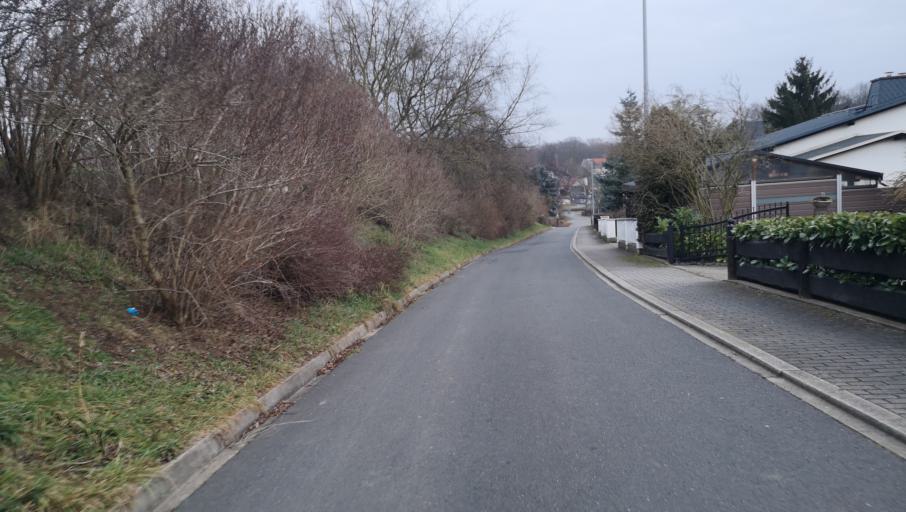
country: DE
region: Thuringia
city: Ronneburg
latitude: 50.8607
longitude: 12.1735
